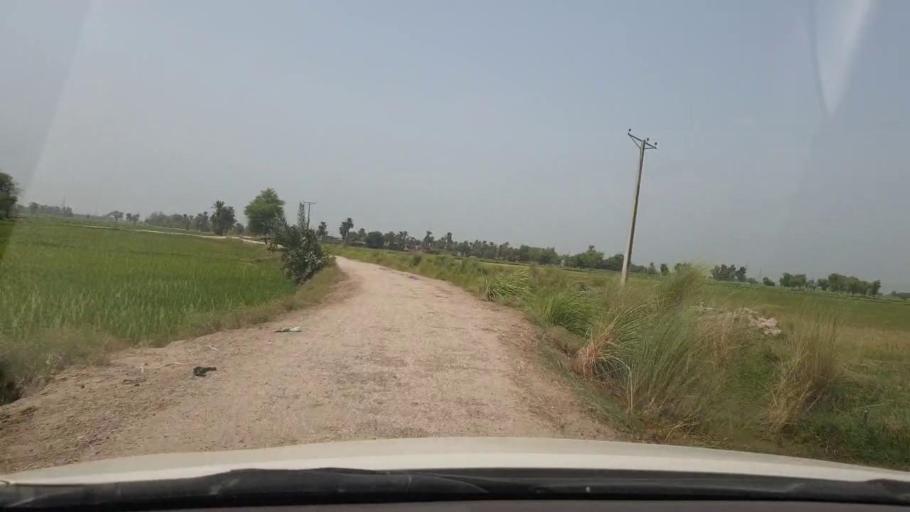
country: PK
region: Sindh
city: Shikarpur
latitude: 28.0116
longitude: 68.6482
